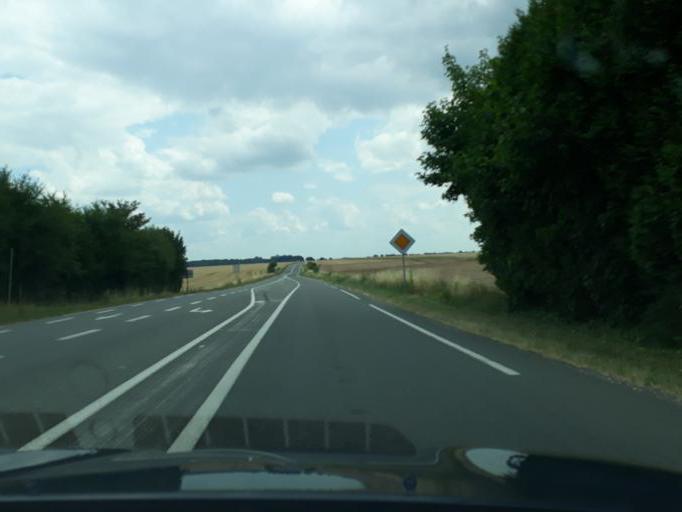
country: FR
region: Centre
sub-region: Departement du Cher
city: Avord
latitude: 47.0305
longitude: 2.6530
